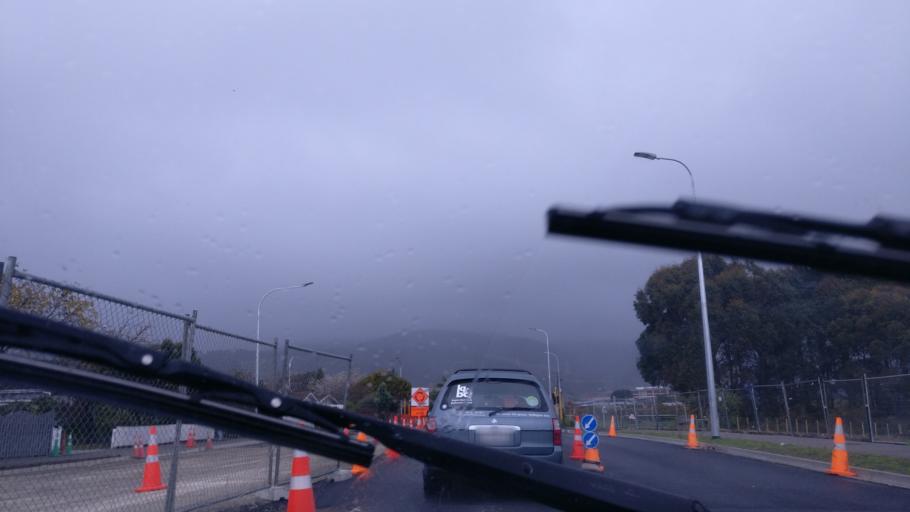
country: NZ
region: Wellington
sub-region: Kapiti Coast District
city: Paraparaumu
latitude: -40.9095
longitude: 175.0006
